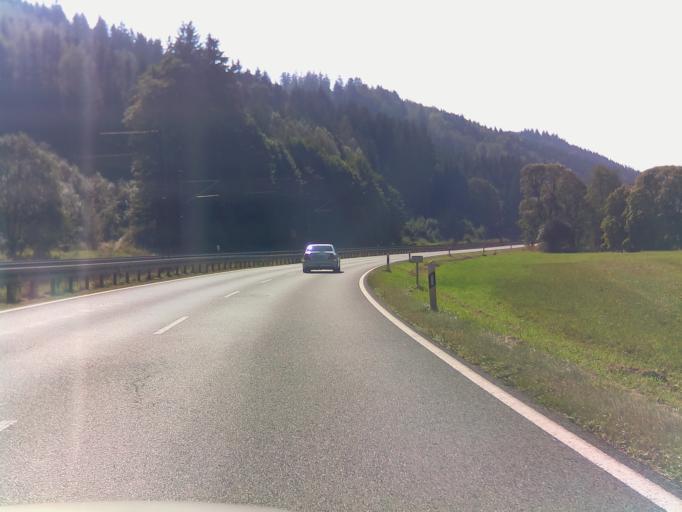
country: DE
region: Bavaria
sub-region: Upper Franconia
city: Teuschnitz
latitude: 50.3840
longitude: 11.3459
